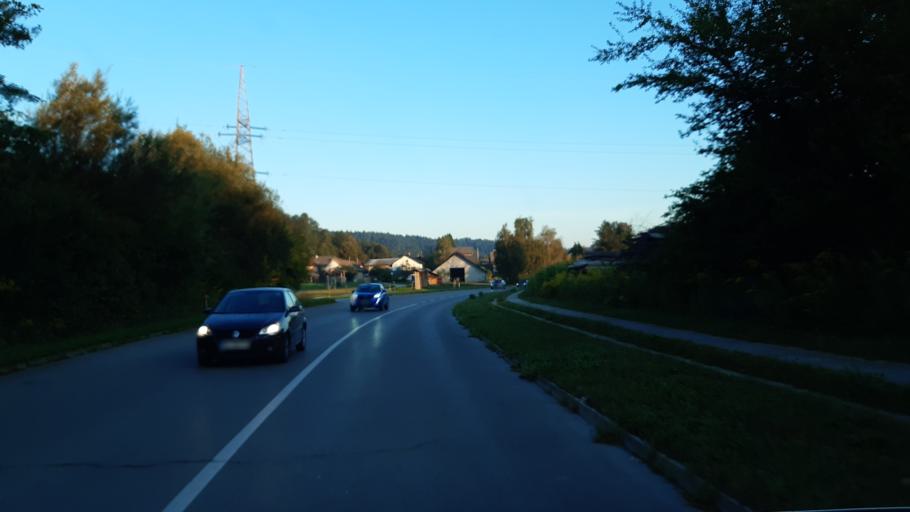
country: SI
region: Medvode
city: Zgornje Pirnice
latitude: 46.1032
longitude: 14.4456
